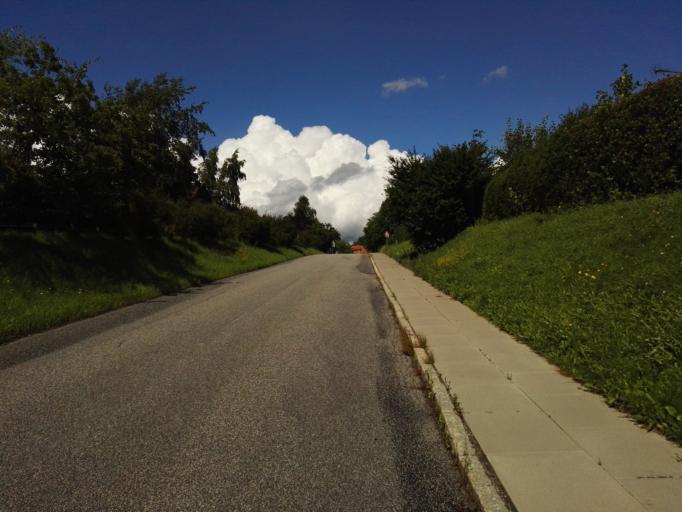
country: DK
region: Capital Region
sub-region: Egedal Kommune
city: Vekso
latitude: 55.7518
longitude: 12.2384
